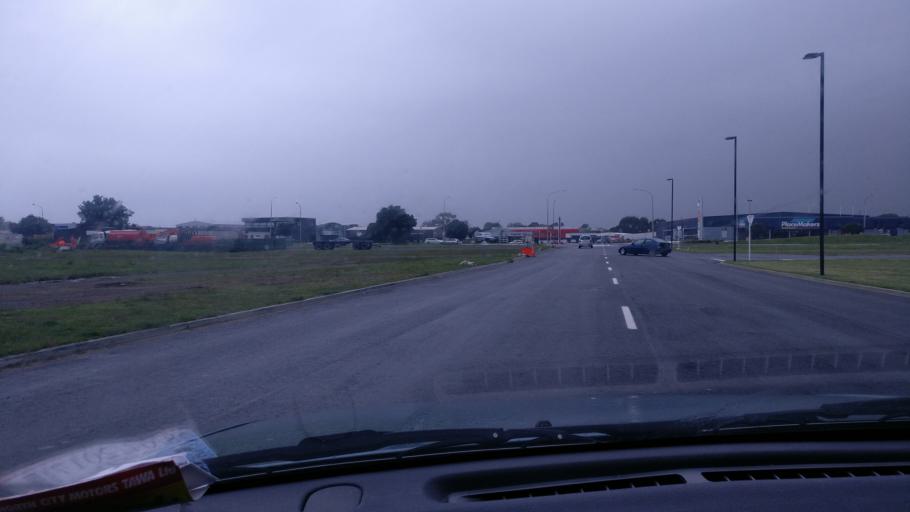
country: NZ
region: Wellington
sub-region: Kapiti Coast District
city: Paraparaumu
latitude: -40.9048
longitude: 174.9935
